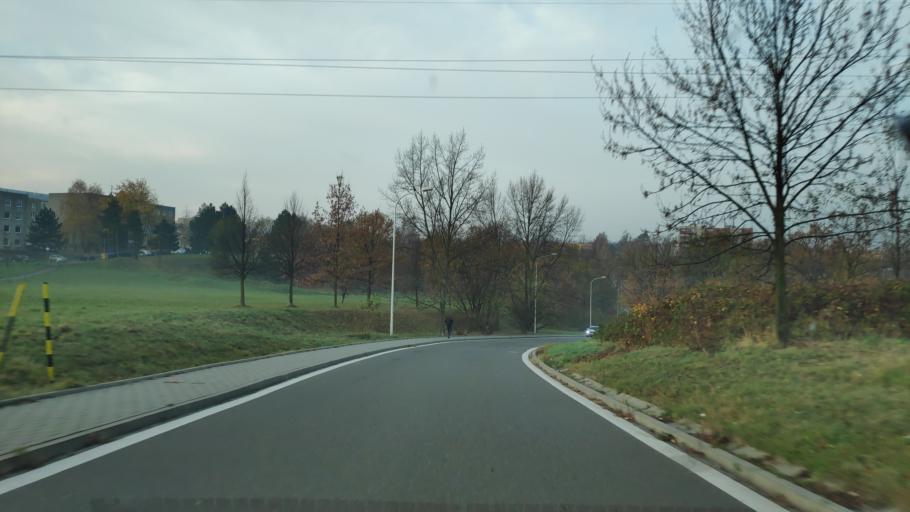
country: CZ
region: Moravskoslezsky
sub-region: Okres Frydek-Mistek
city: Frydek-Mistek
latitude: 49.6954
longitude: 18.3467
